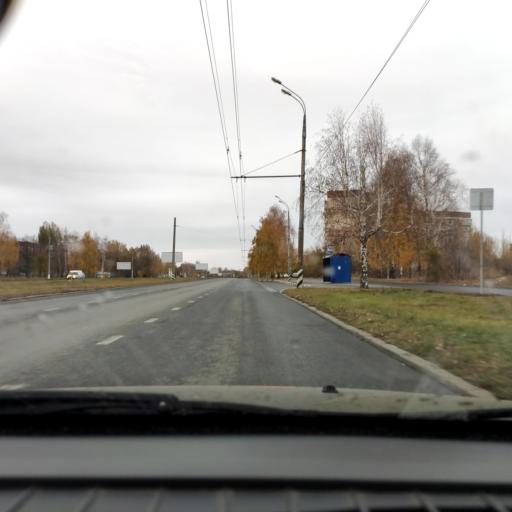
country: RU
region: Samara
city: Tol'yatti
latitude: 53.5040
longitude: 49.2574
